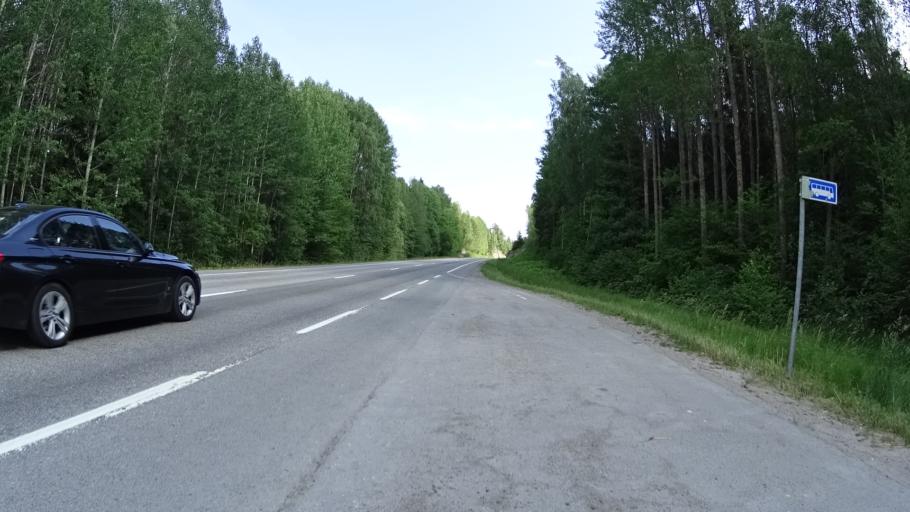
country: FI
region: Uusimaa
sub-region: Raaseporin
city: Karis
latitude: 60.0931
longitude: 23.6355
